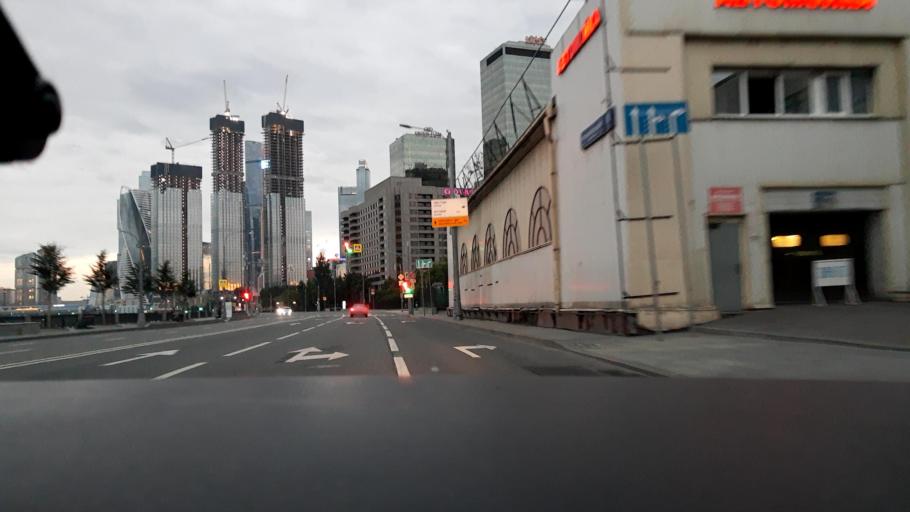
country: RU
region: Moskovskaya
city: Novopodrezkovo
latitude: 55.9757
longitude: 37.4102
